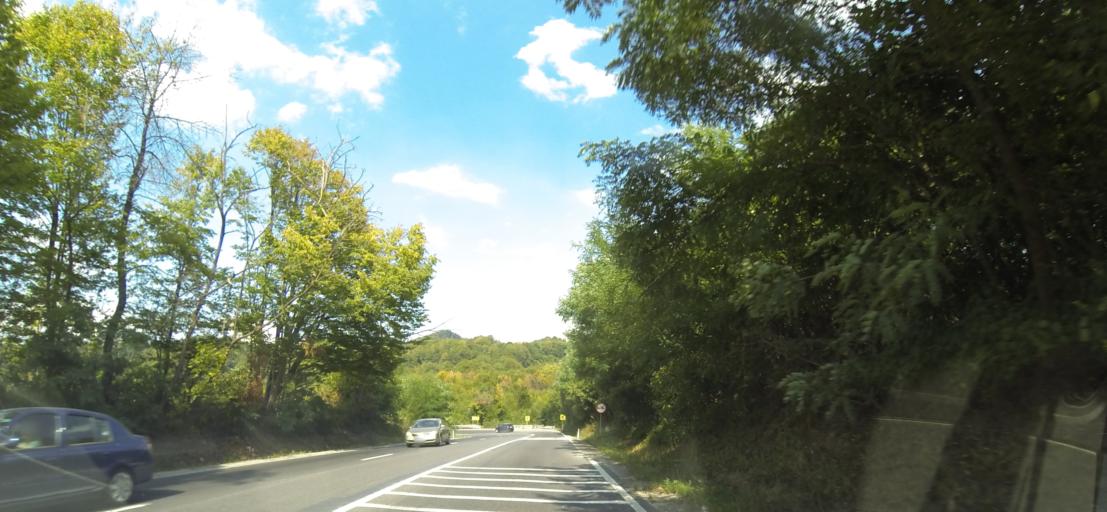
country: RO
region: Brasov
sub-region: Comuna Sinca Noua
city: Sinca Noua
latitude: 45.7543
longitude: 25.2752
